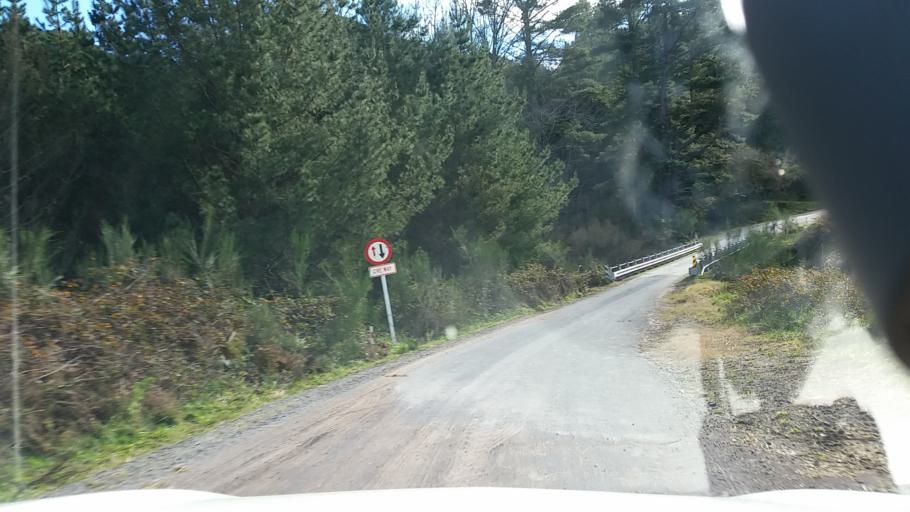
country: NZ
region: Bay of Plenty
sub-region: Rotorua District
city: Rotorua
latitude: -38.3771
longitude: 176.2012
